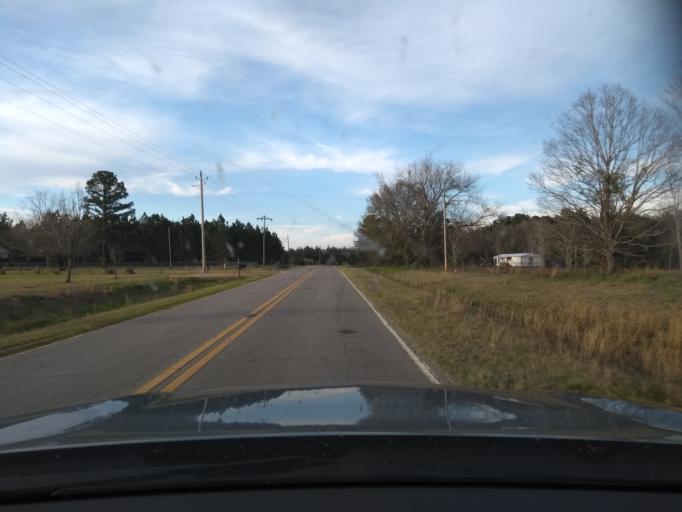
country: US
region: Georgia
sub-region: Evans County
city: Claxton
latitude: 32.2319
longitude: -81.7709
